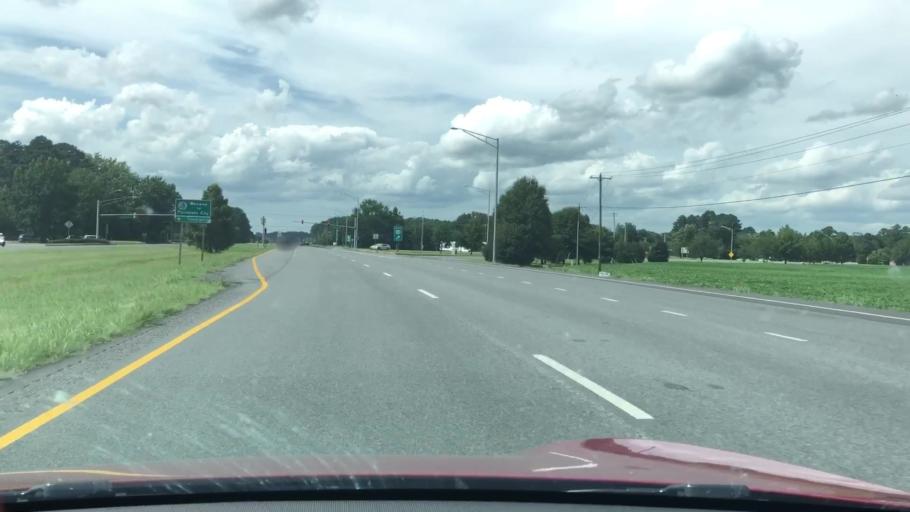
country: US
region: Maryland
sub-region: Worcester County
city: Pocomoke City
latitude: 38.0648
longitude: -75.5458
